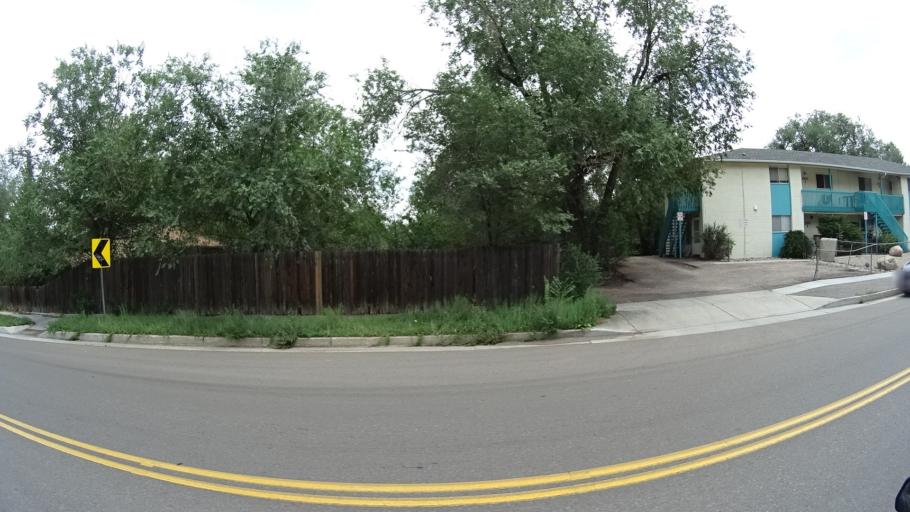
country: US
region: Colorado
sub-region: El Paso County
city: Colorado Springs
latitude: 38.8706
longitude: -104.8359
